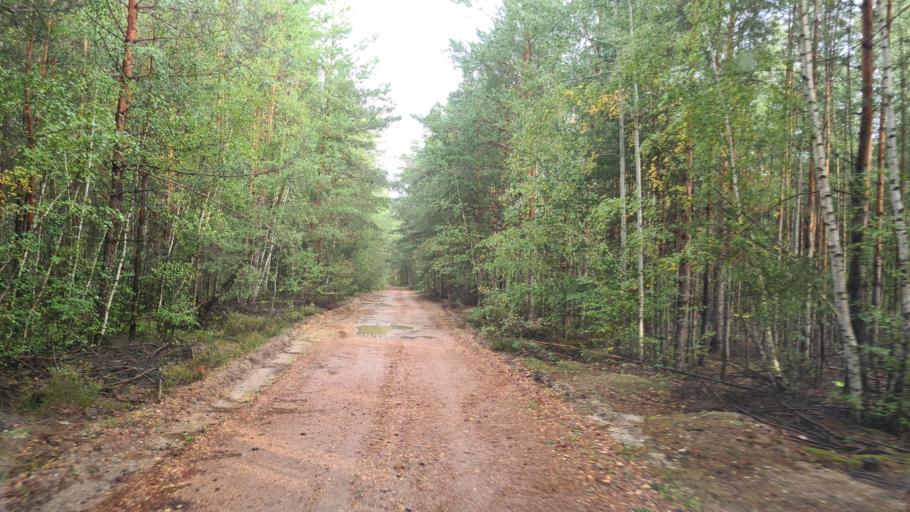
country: DE
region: Brandenburg
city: Sallgast
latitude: 51.5882
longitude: 13.8007
